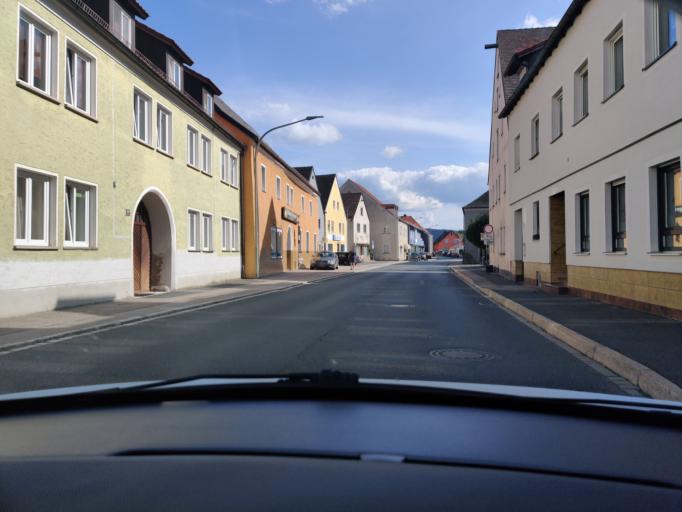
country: DE
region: Bavaria
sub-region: Upper Palatinate
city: Nabburg
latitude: 49.4540
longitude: 12.1848
